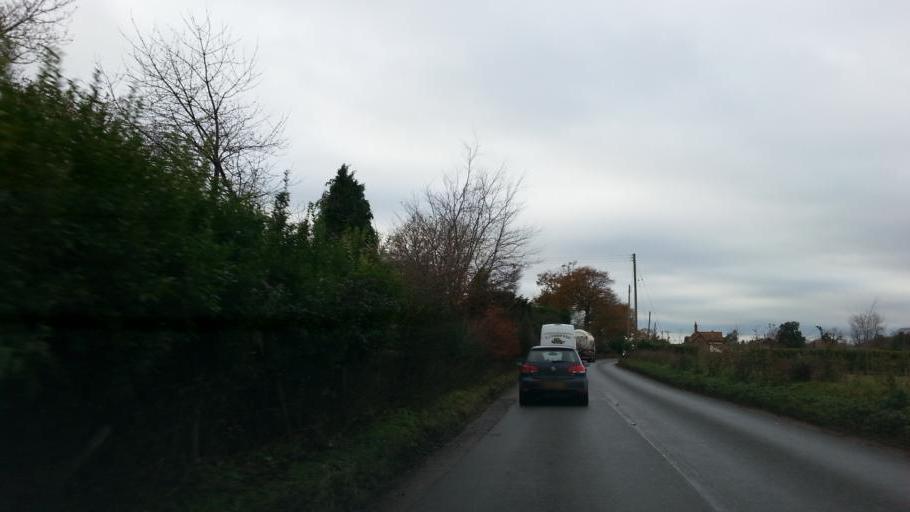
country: GB
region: England
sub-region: Norfolk
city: Diss
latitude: 52.3570
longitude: 1.1876
